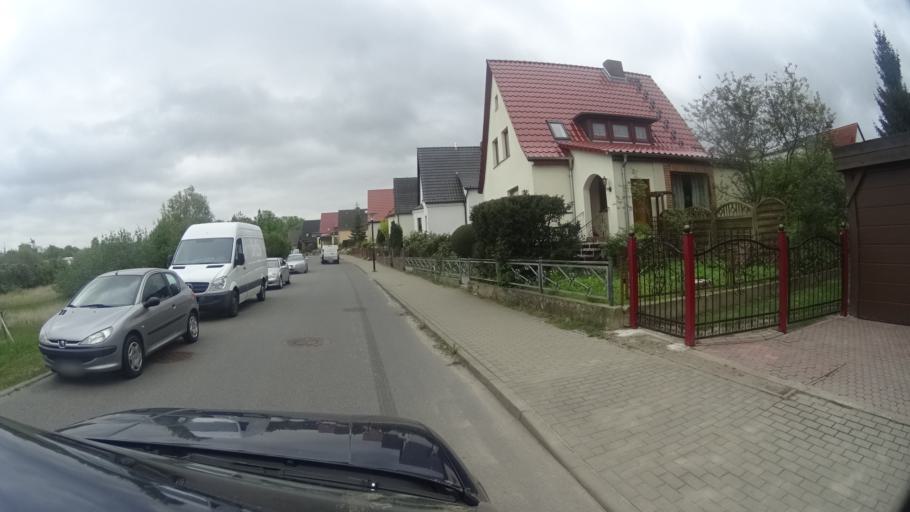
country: DE
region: Mecklenburg-Vorpommern
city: Ribnitz-Damgarten
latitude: 54.2420
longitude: 12.4227
